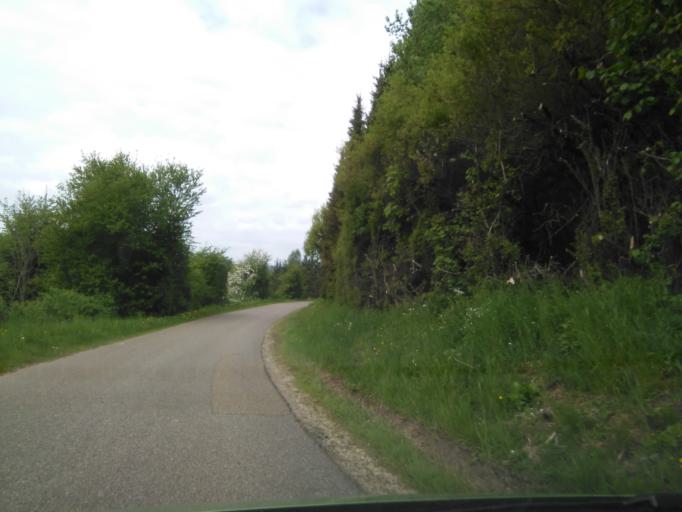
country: DK
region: Central Jutland
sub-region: Skanderborg Kommune
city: Ry
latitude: 56.0647
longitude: 9.8343
